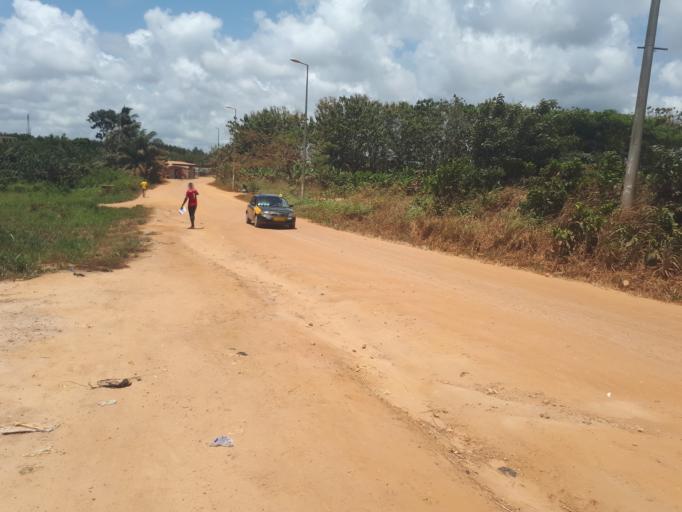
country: GH
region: Central
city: Cape Coast
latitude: 5.1228
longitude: -1.2953
